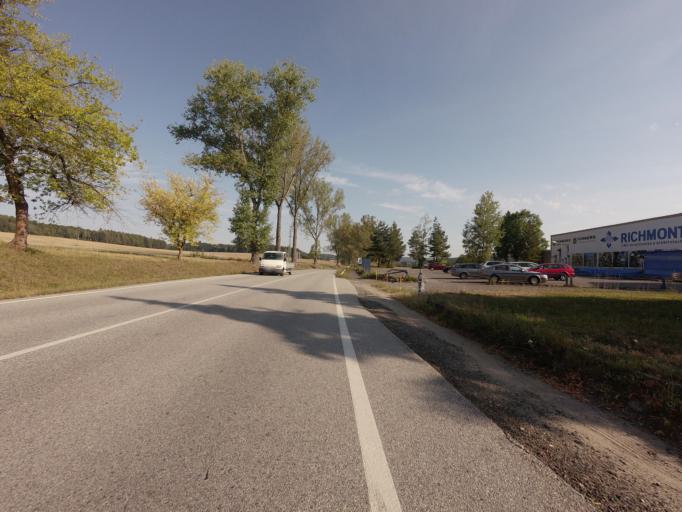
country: CZ
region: Jihocesky
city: Tyn nad Vltavou
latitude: 49.2331
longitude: 14.4213
